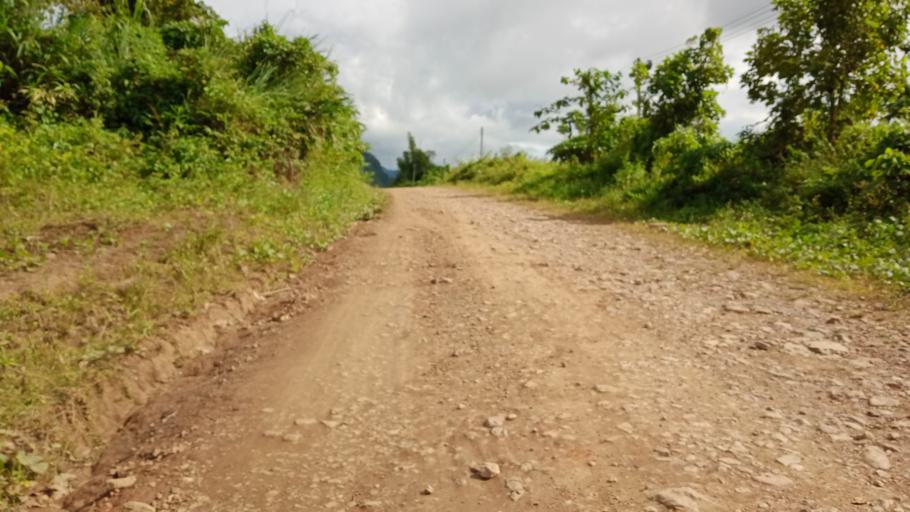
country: LA
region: Xiangkhoang
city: Phonsavan
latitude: 19.1072
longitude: 102.9287
